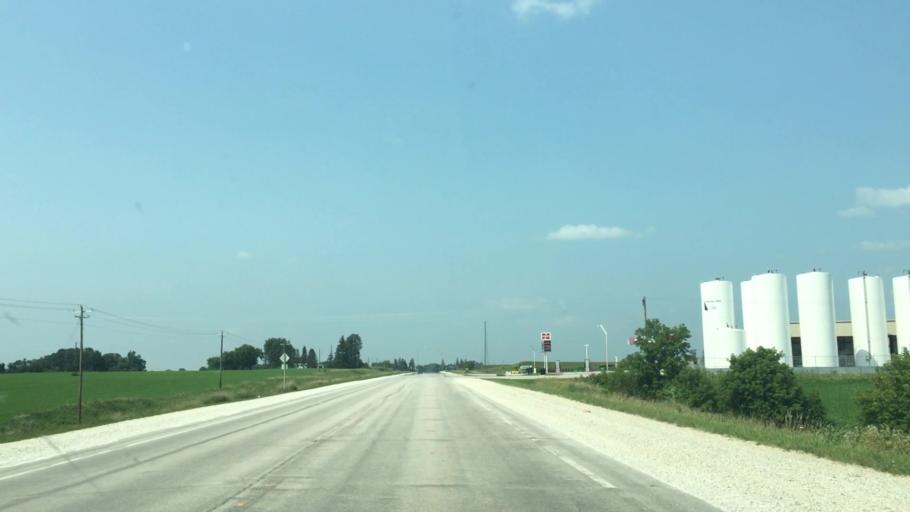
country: US
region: Iowa
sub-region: Winneshiek County
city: Decorah
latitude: 43.4376
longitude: -91.8611
